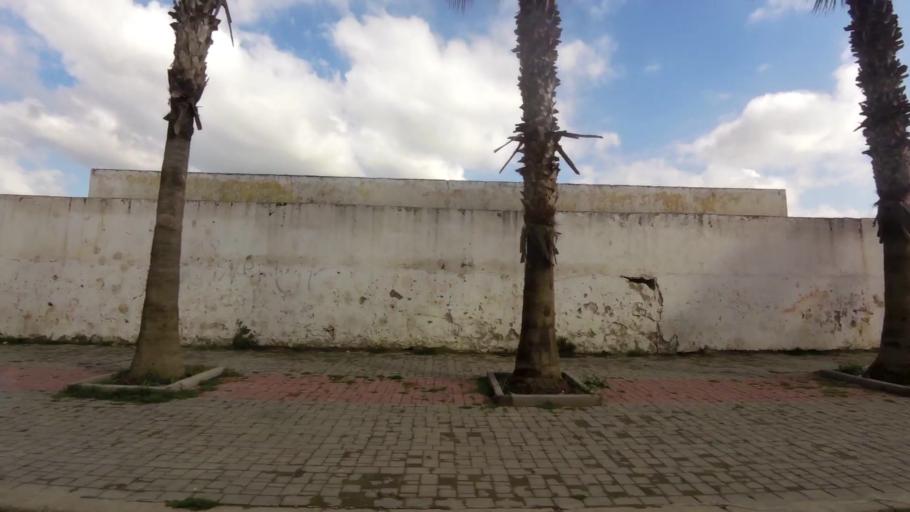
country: MA
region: Chaouia-Ouardigha
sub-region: Settat Province
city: Berrechid
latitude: 33.2719
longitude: -7.5684
